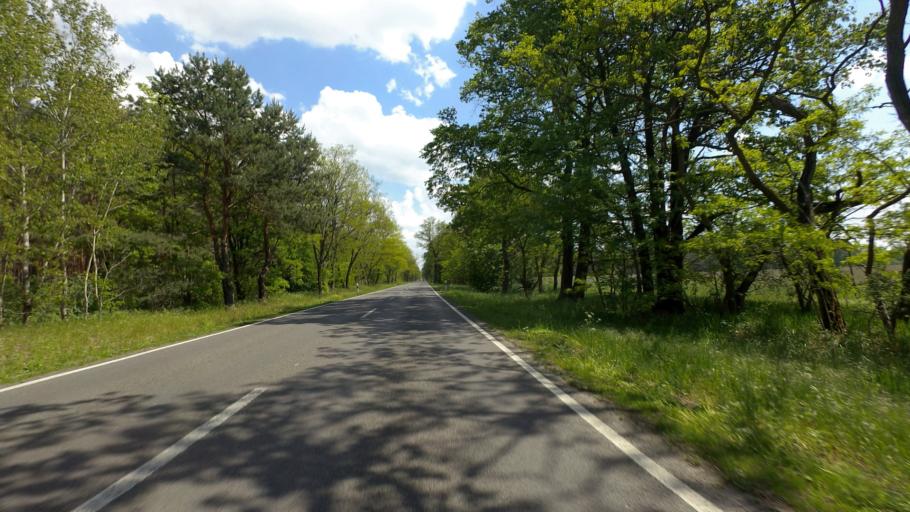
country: DE
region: Brandenburg
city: Luebben
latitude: 51.9426
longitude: 13.9324
